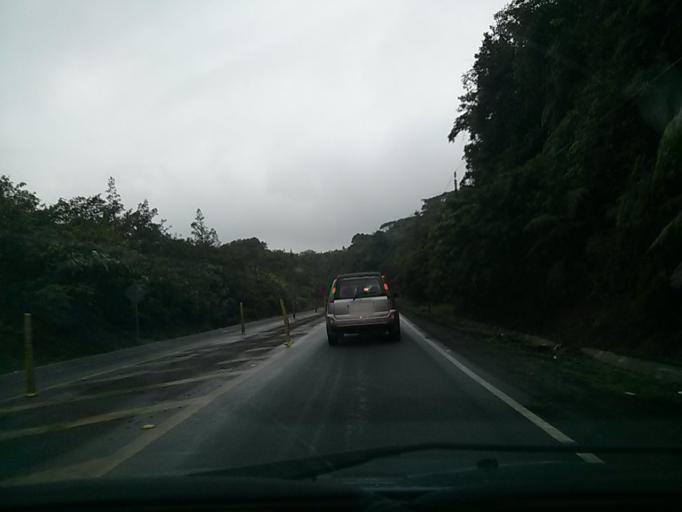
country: CR
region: Heredia
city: Angeles
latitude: 10.0513
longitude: -84.0045
